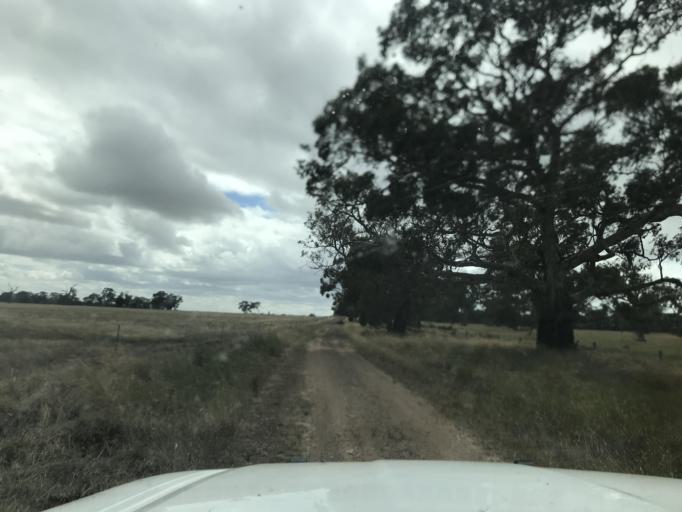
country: AU
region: South Australia
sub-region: Naracoorte and Lucindale
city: Naracoorte
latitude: -36.9012
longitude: 141.4093
